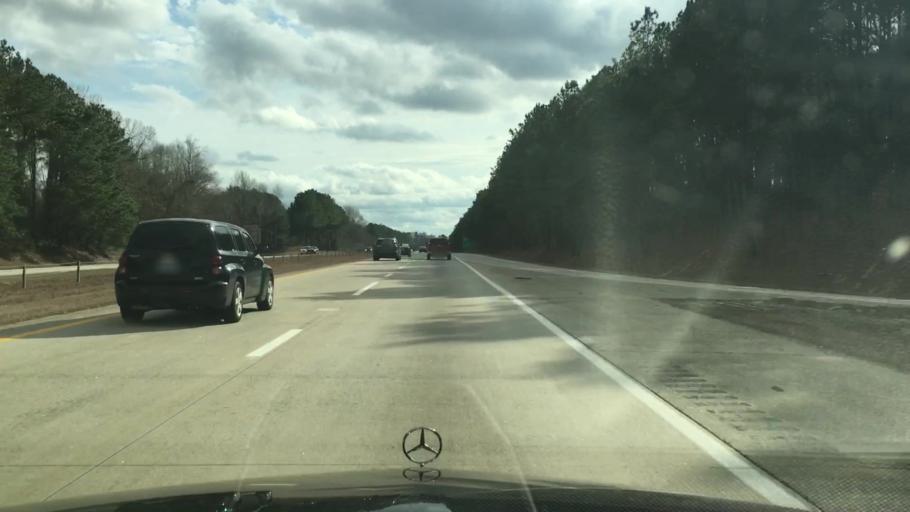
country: US
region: North Carolina
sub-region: Johnston County
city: Benson
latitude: 35.4206
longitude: -78.5292
